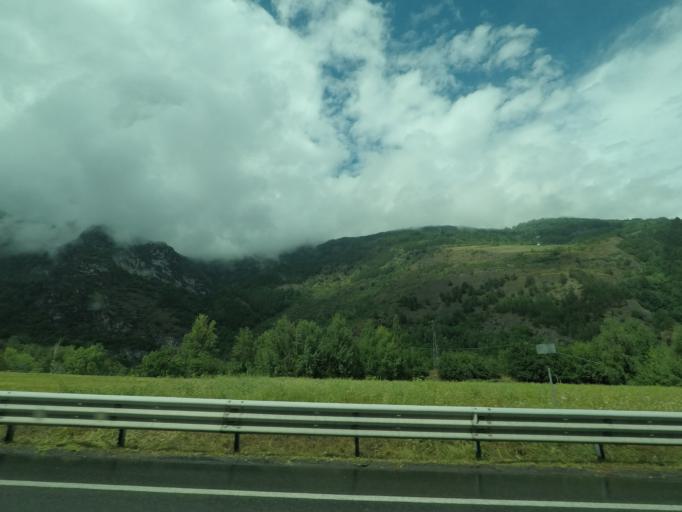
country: IT
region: Aosta Valley
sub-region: Valle d'Aosta
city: Introd
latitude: 45.7031
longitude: 7.1835
